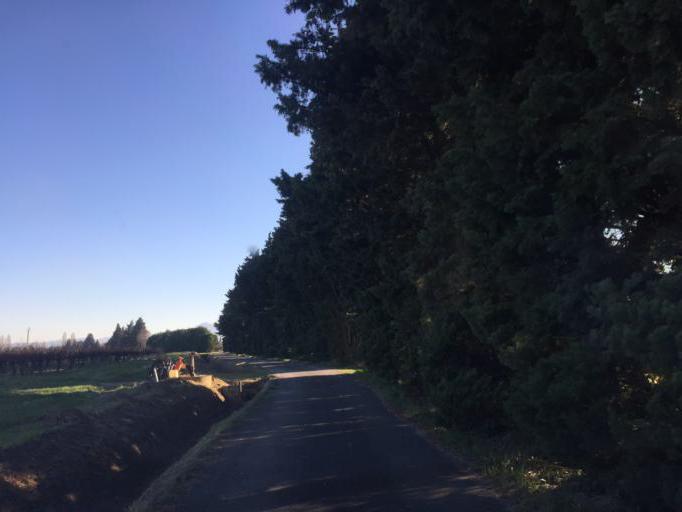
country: FR
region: Provence-Alpes-Cote d'Azur
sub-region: Departement du Vaucluse
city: Orange
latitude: 44.1509
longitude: 4.8202
